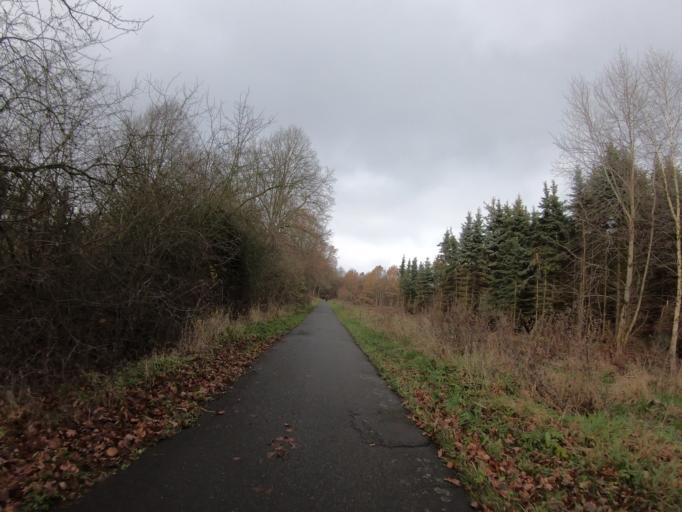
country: DE
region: Lower Saxony
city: Wagenhoff
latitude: 52.5384
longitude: 10.5206
